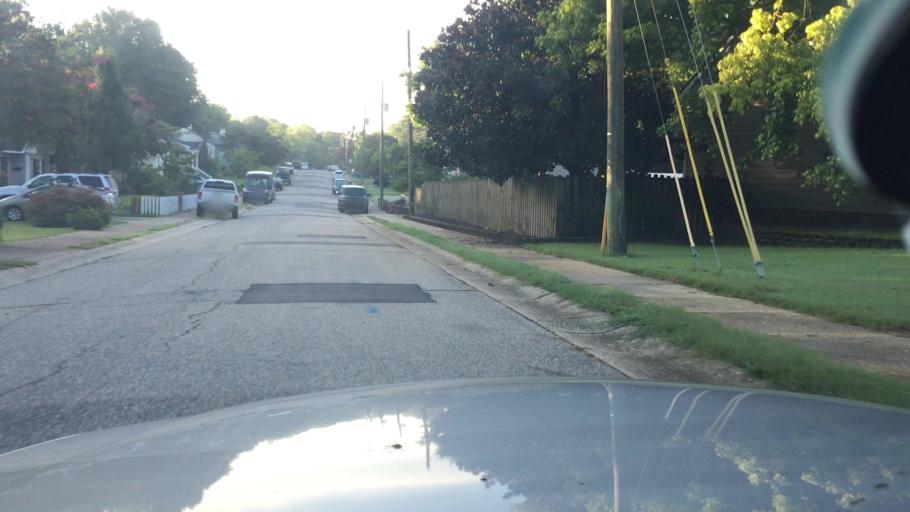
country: US
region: North Carolina
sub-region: Cumberland County
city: Fayetteville
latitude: 35.0615
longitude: -78.9051
